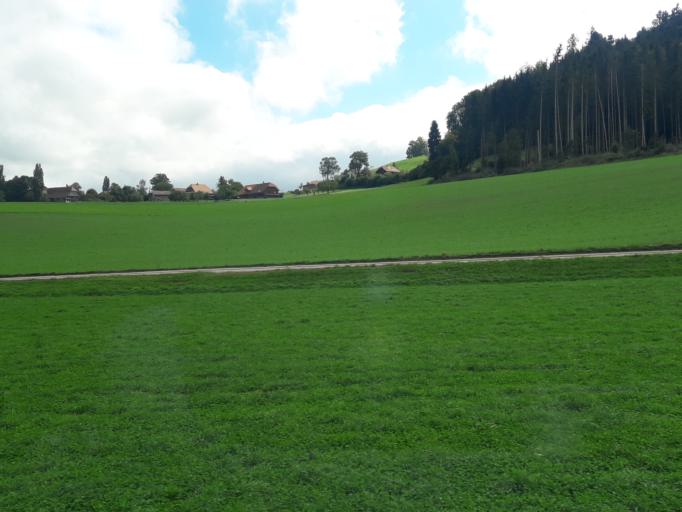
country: CH
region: Bern
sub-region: Bern-Mittelland District
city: Wahlern
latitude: 46.8396
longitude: 7.3453
